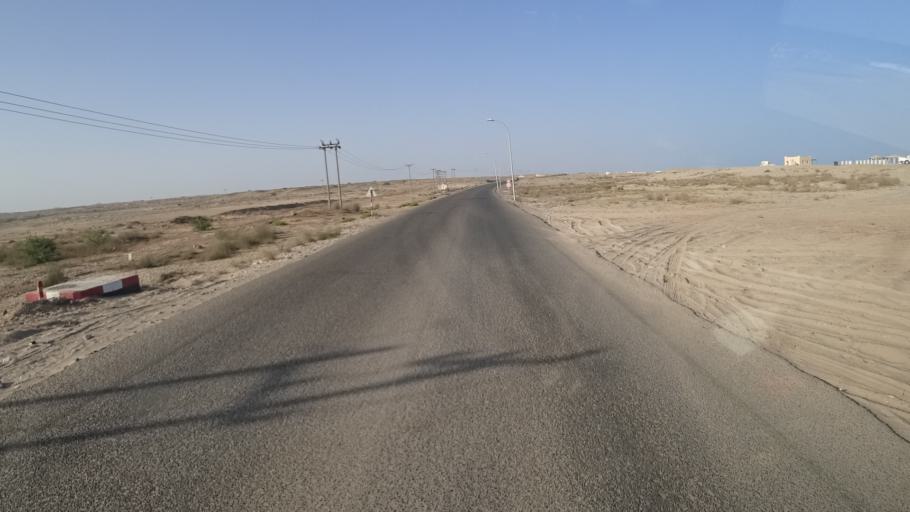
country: OM
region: Ash Sharqiyah
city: Sur
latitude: 22.1325
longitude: 59.7269
